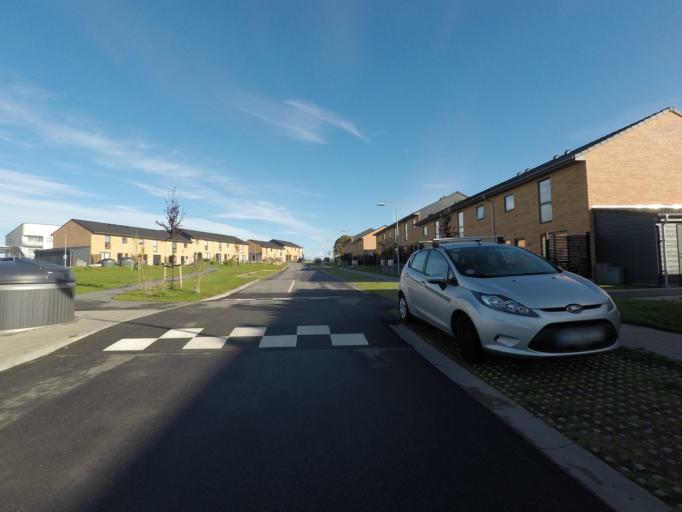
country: DK
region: Capital Region
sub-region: Egedal Kommune
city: Smorumnedre
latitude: 55.7452
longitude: 12.2888
